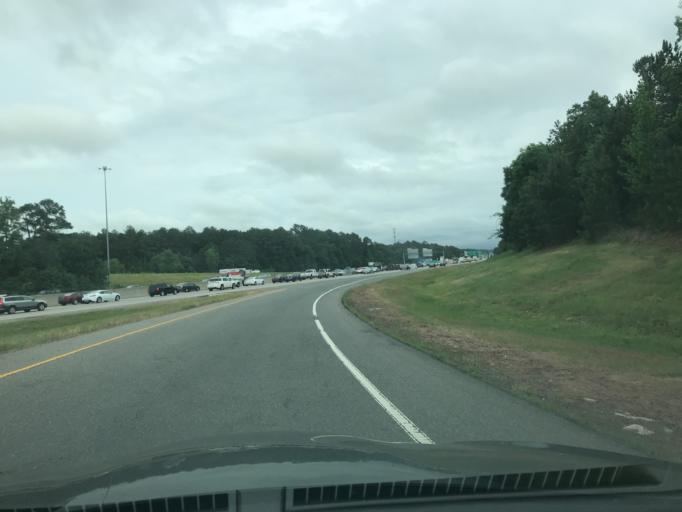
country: US
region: North Carolina
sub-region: Wake County
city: Morrisville
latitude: 35.8712
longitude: -78.8301
